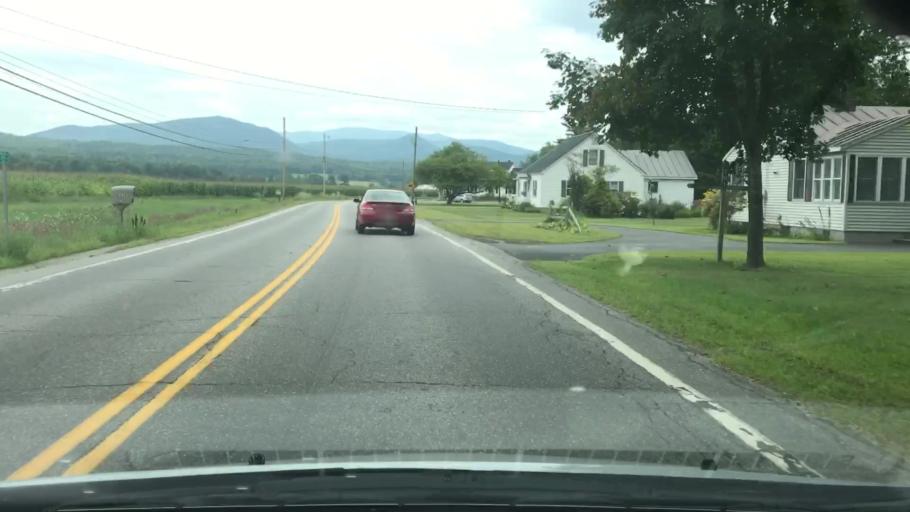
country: US
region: New Hampshire
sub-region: Grafton County
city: North Haverhill
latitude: 44.1036
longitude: -72.0305
